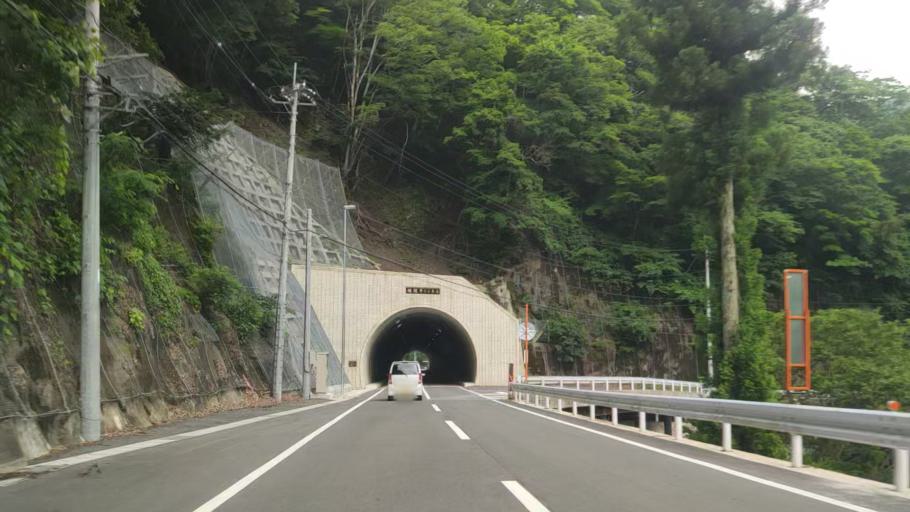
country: JP
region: Gunma
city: Tomioka
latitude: 36.0882
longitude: 138.7199
